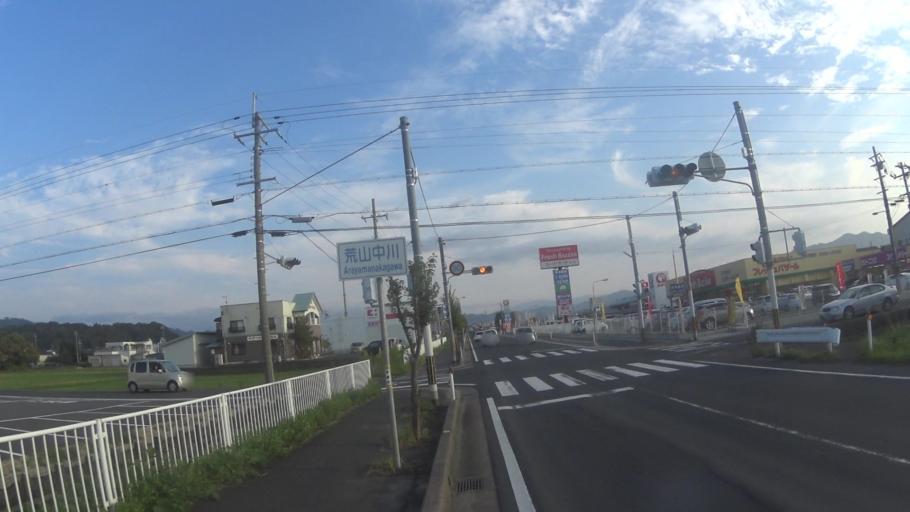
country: JP
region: Kyoto
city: Miyazu
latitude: 35.6179
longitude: 135.0761
